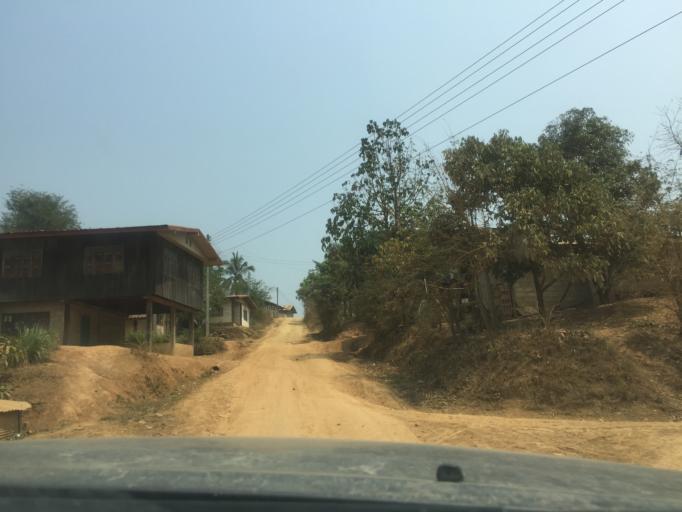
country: LA
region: Xiagnabouli
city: Muang Kenthao
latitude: 17.7836
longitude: 101.2408
